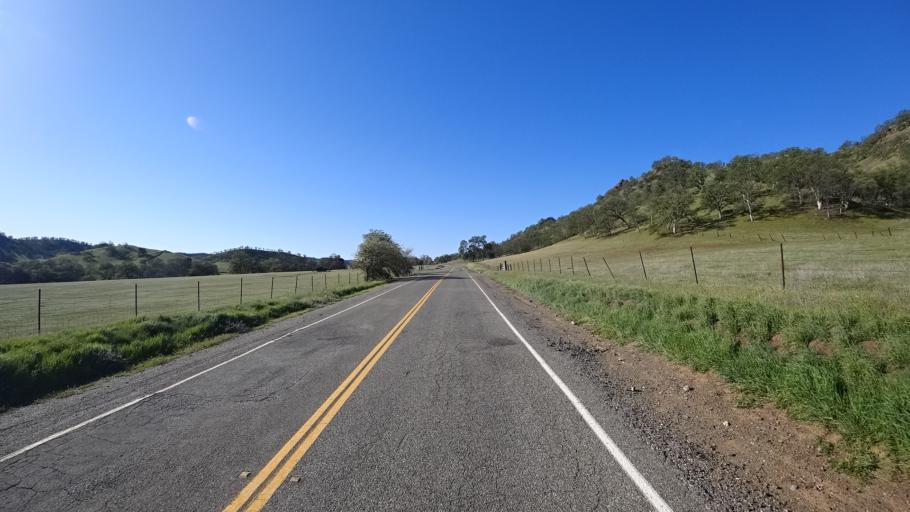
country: US
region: California
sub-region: Tehama County
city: Rancho Tehama Reserve
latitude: 39.7778
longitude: -122.5212
